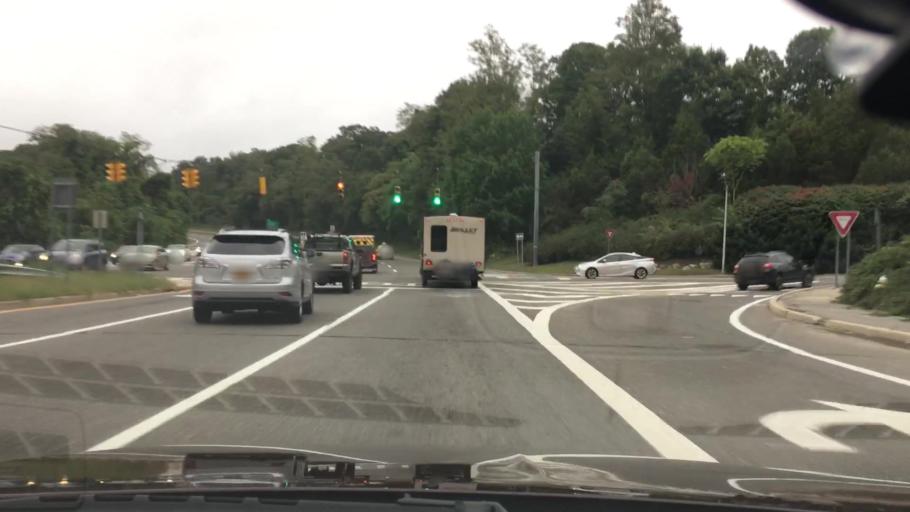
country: US
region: New York
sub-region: Suffolk County
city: Setauket-East Setauket
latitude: 40.9249
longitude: -73.1197
